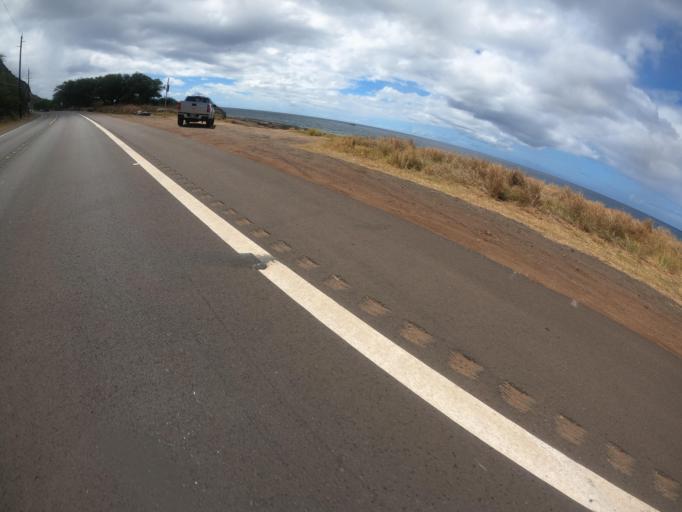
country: US
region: Hawaii
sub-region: Honolulu County
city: Makaha Valley
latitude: 21.5011
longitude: -158.2296
